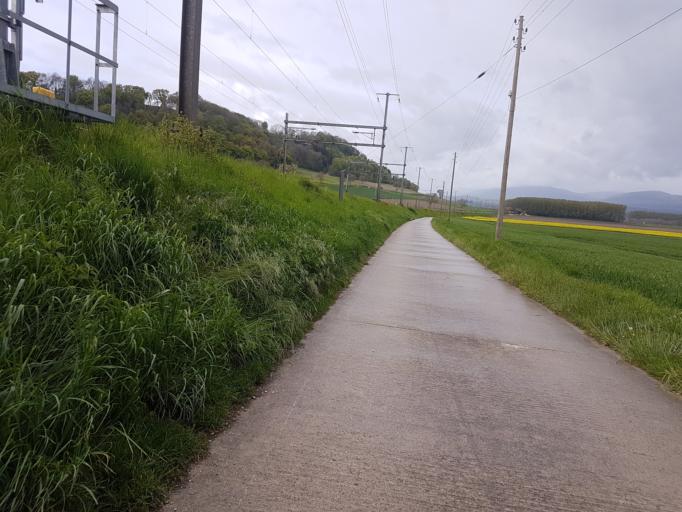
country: CH
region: Vaud
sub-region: Jura-Nord vaudois District
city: Montagny
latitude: 46.7457
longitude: 6.6057
